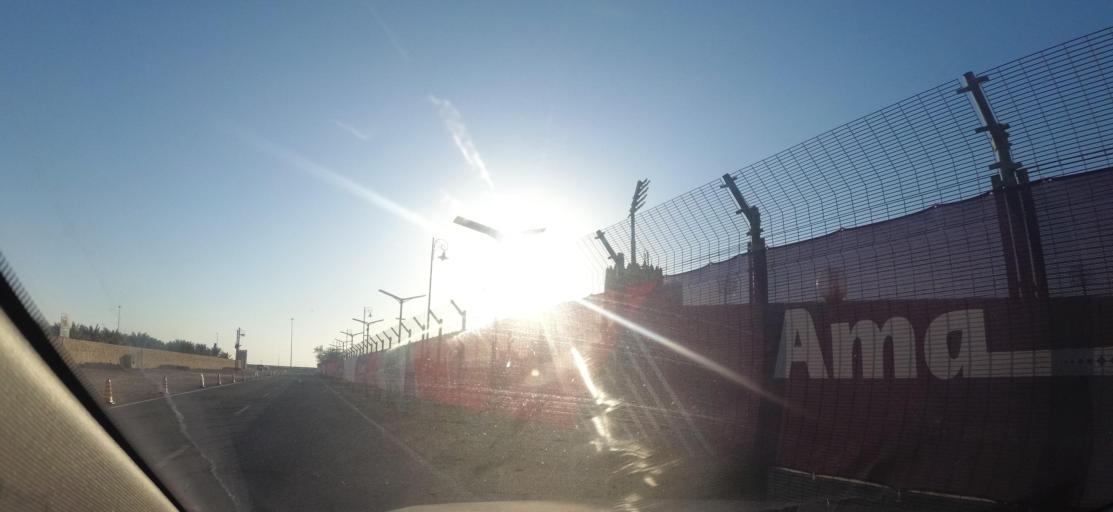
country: QA
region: Madinat ash Shamal
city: Ar Ru'ays
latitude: 26.1177
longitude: 51.2226
